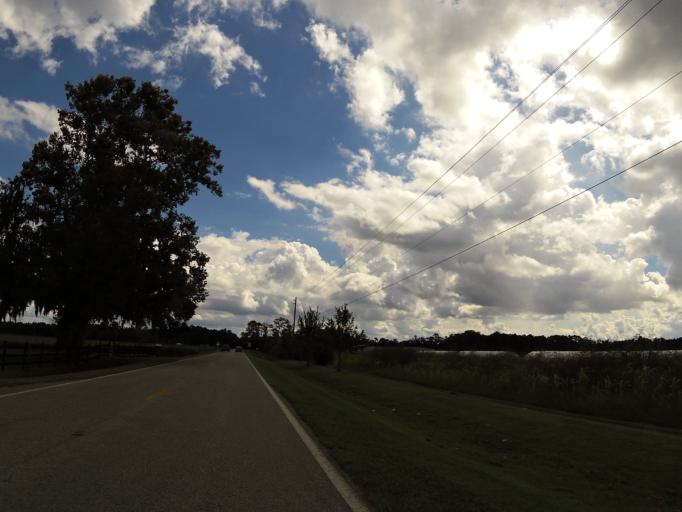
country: US
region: Florida
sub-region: Putnam County
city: East Palatka
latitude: 29.7536
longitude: -81.4758
